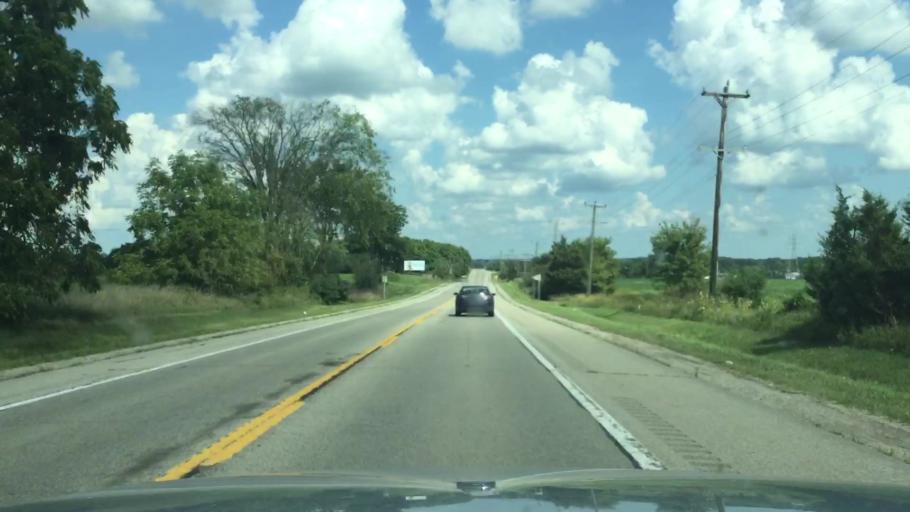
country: US
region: Michigan
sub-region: Washtenaw County
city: Saline
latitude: 42.1534
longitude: -83.8135
